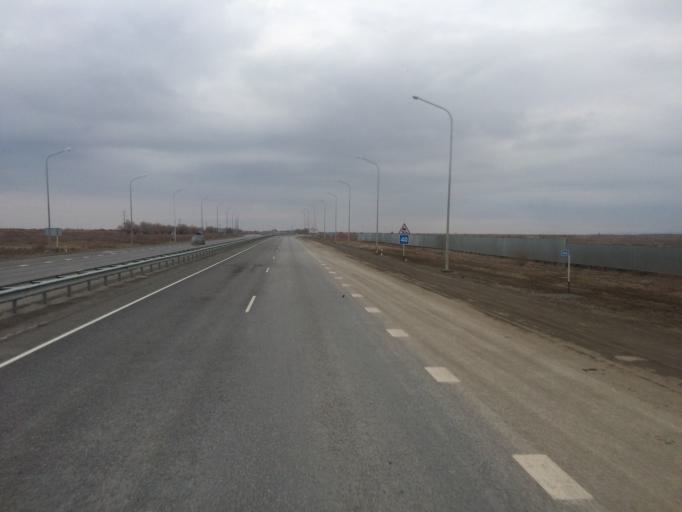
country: KZ
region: Qyzylorda
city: Shieli
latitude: 44.1404
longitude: 66.9640
